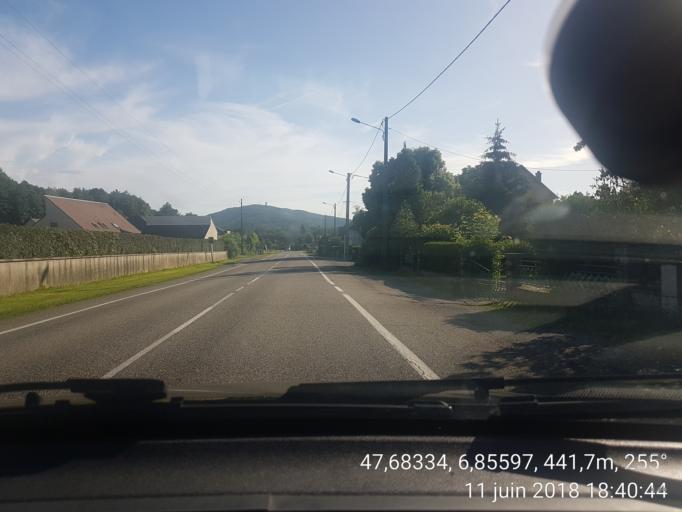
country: FR
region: Franche-Comte
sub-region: Territoire de Belfort
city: Valdoie
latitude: 47.6831
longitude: 6.8557
